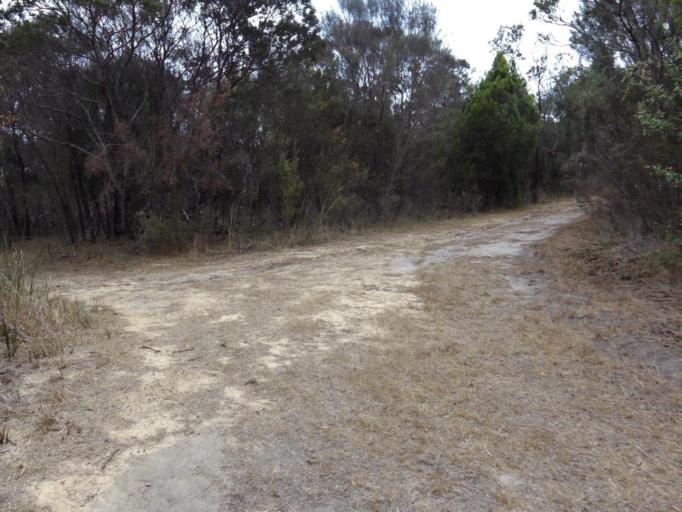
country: AU
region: Victoria
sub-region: Mornington Peninsula
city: Safety Beach
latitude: -38.2925
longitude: 144.9995
